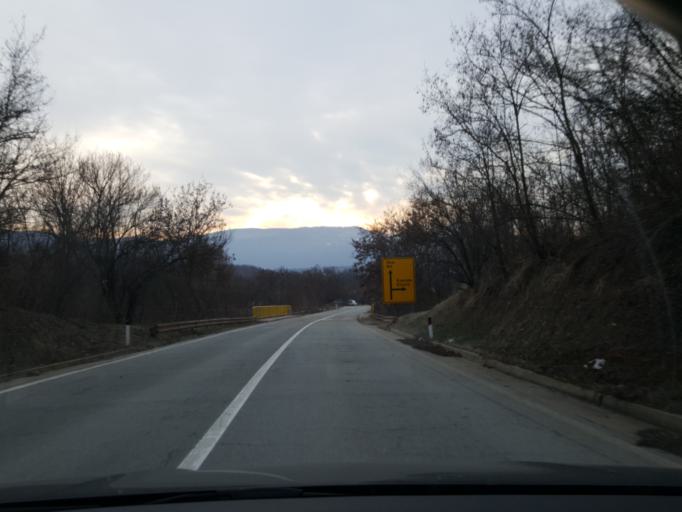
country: RS
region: Central Serbia
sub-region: Pirotski Okrug
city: Bela Palanka
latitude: 43.2233
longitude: 22.3649
